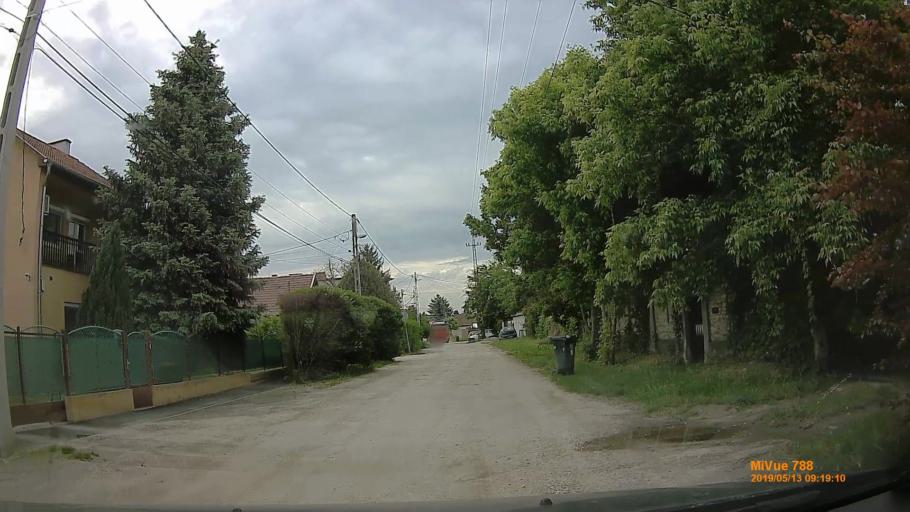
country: HU
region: Budapest
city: Budapest XXI. keruelet
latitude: 47.4029
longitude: 19.0845
